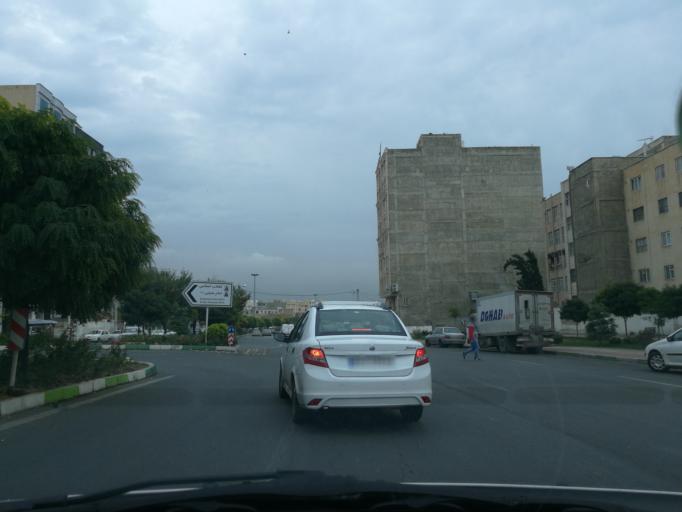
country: IR
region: Alborz
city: Karaj
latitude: 35.8522
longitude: 50.9640
